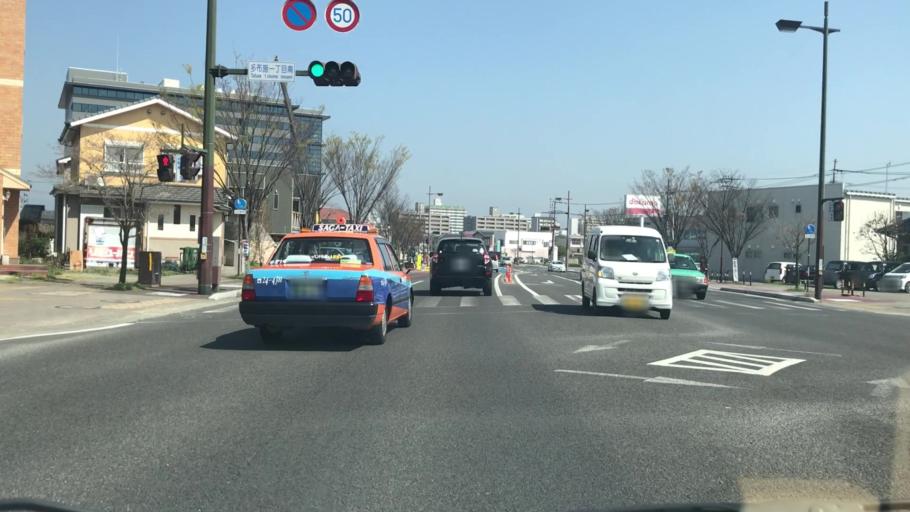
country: JP
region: Saga Prefecture
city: Saga-shi
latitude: 33.2539
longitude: 130.2924
